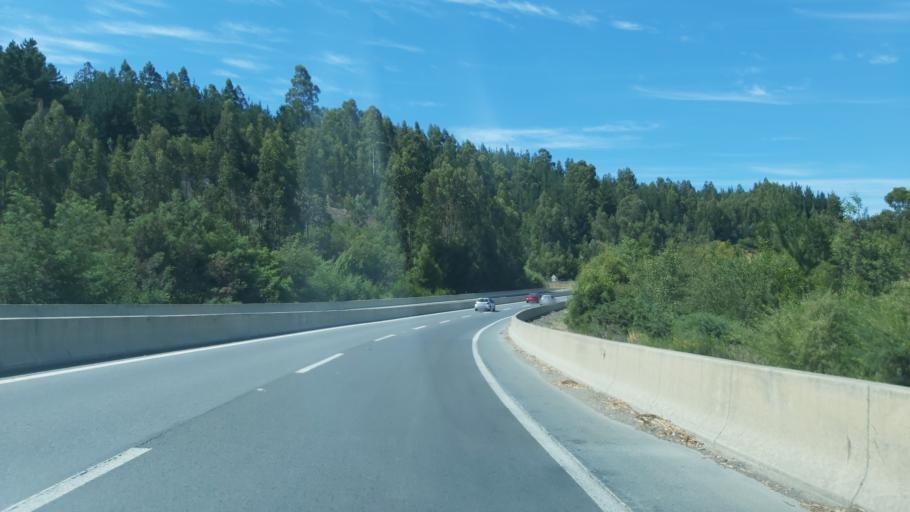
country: CL
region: Biobio
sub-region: Provincia de Concepcion
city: Lota
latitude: -37.0735
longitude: -73.1365
